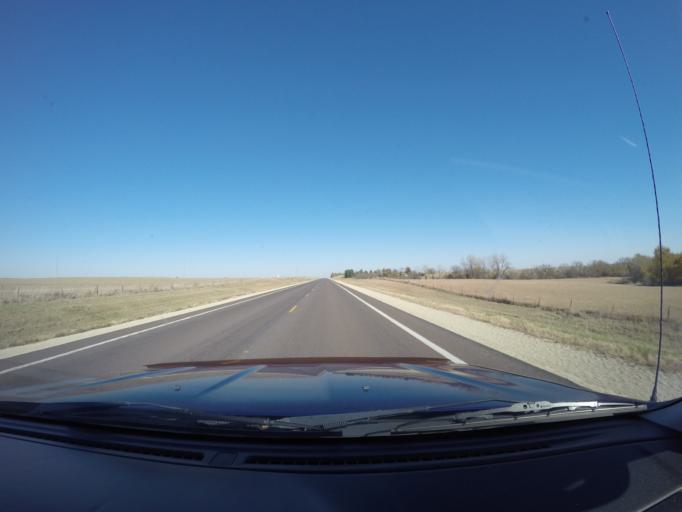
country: US
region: Kansas
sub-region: Marshall County
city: Blue Rapids
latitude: 39.6510
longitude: -96.7505
